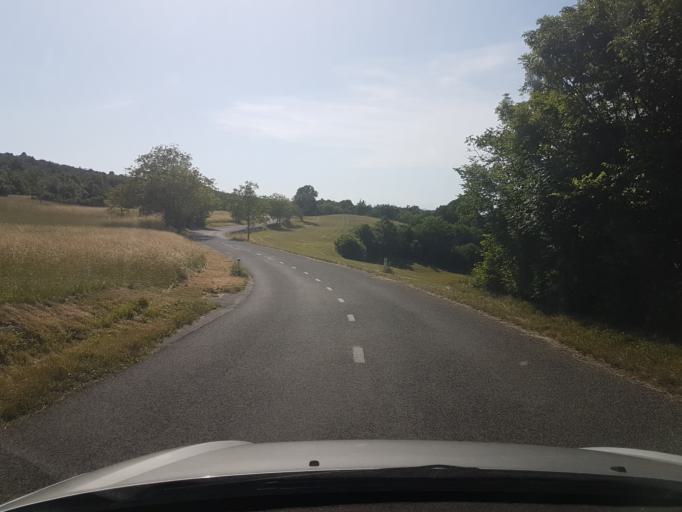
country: SI
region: Vipava
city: Vipava
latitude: 45.7725
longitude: 13.9546
